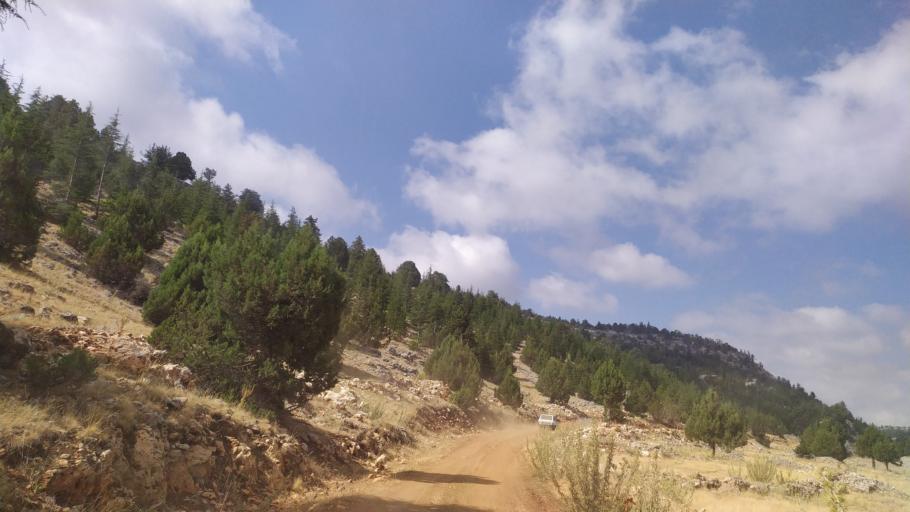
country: TR
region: Mersin
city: Kirobasi
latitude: 36.6184
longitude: 33.8370
